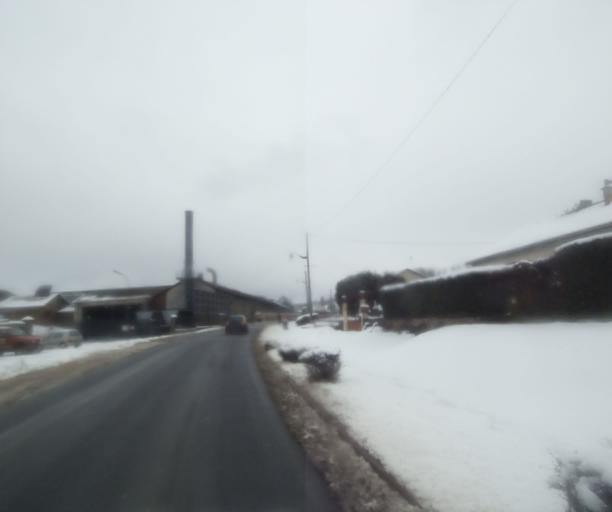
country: FR
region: Champagne-Ardenne
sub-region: Departement de la Haute-Marne
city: Wassy
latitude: 48.4876
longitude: 4.9682
